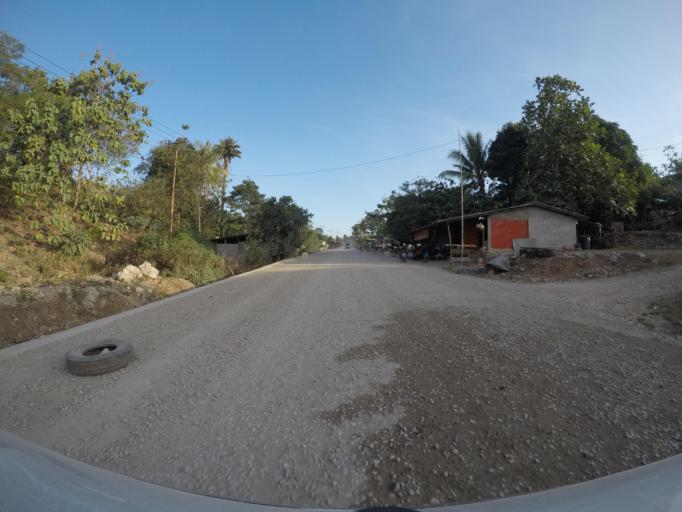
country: TL
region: Viqueque
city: Viqueque
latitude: -8.8343
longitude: 126.5190
